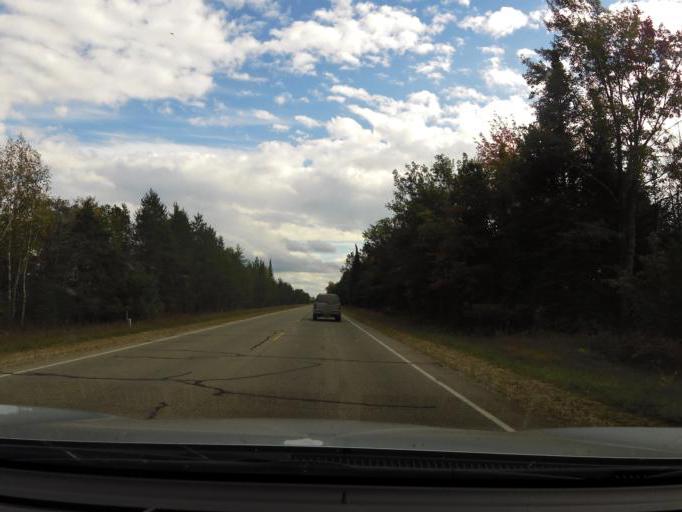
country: US
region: Michigan
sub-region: Roscommon County
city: Roscommon
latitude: 44.4455
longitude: -84.5179
